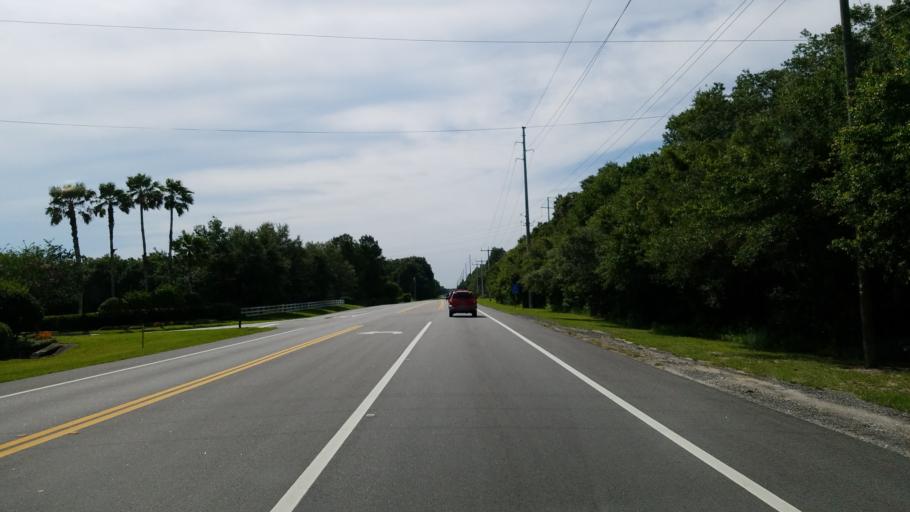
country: US
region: Florida
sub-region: Hillsborough County
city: Fish Hawk
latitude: 27.8534
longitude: -82.1863
